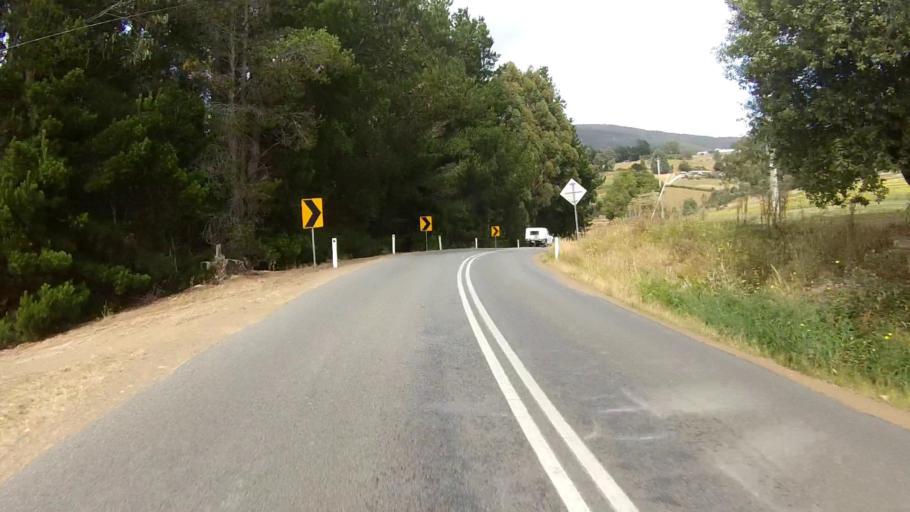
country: AU
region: Tasmania
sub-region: Kingborough
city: Kettering
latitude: -43.1746
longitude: 147.2374
